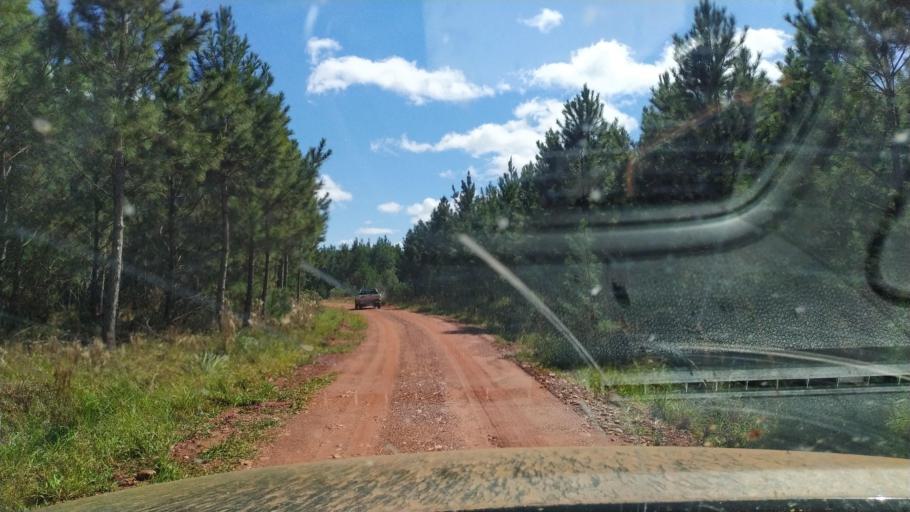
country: AR
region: Corrientes
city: Santo Tome
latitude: -28.4608
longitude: -55.9846
